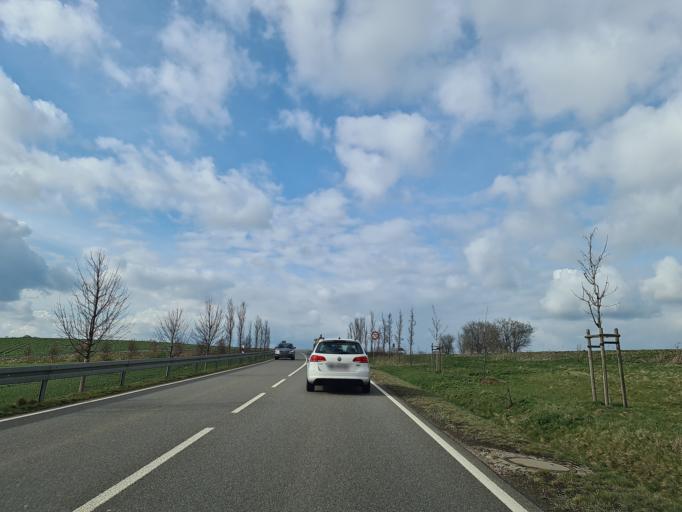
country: DE
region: Saxony
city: Reinsdorf
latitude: 50.6924
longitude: 12.5957
